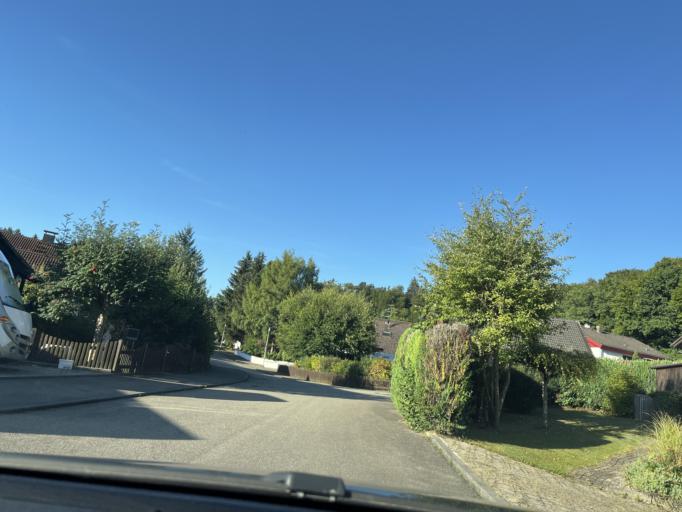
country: DE
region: Baden-Wuerttemberg
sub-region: Tuebingen Region
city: Gammertingen
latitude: 48.2413
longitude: 9.2096
